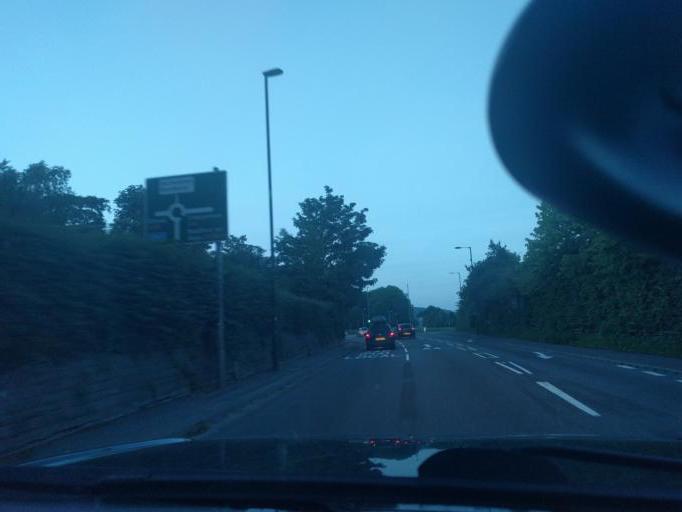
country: GB
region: England
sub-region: Bath and North East Somerset
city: Bath
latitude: 51.3978
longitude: -2.3385
